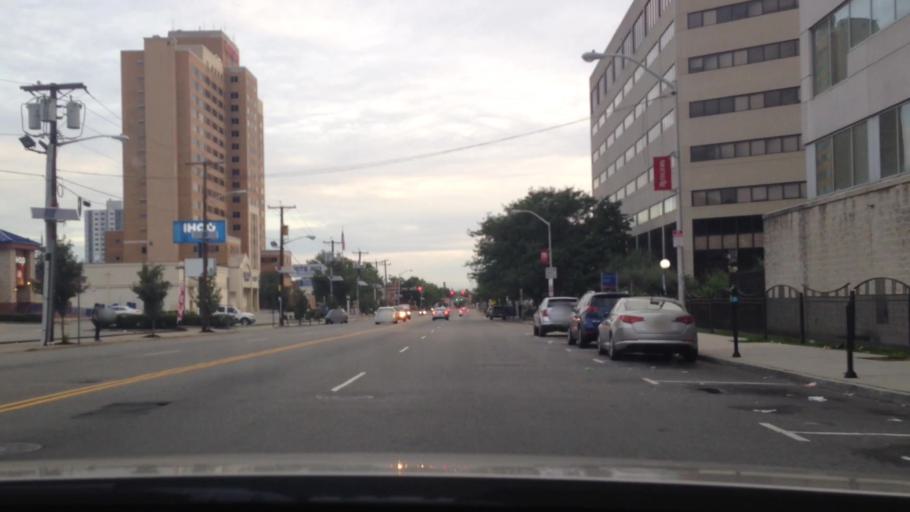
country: US
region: New Jersey
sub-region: Essex County
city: Newark
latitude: 40.7408
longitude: -74.1922
